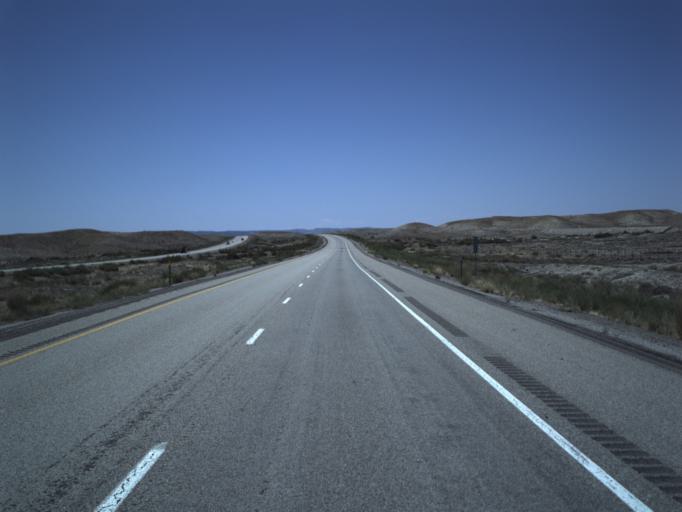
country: US
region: Utah
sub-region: Grand County
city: Moab
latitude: 38.9997
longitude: -109.3218
